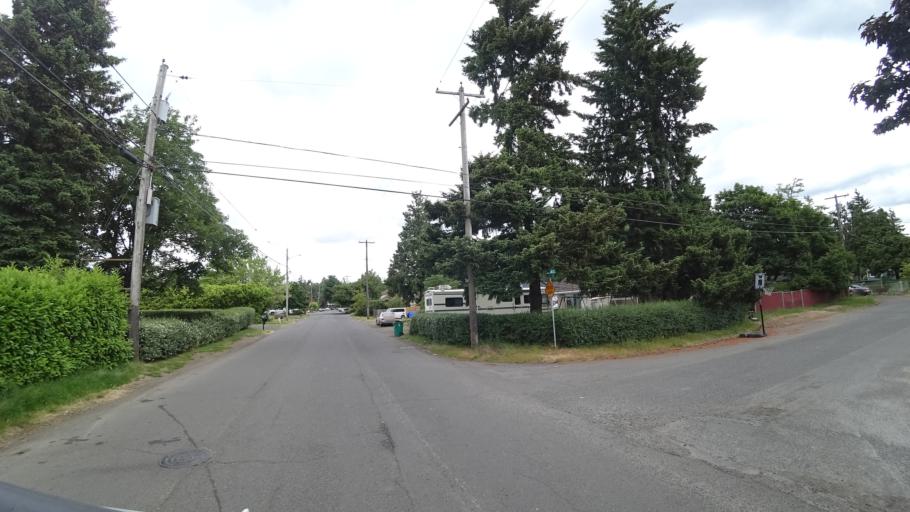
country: US
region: Oregon
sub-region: Multnomah County
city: Lents
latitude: 45.4947
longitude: -122.5300
